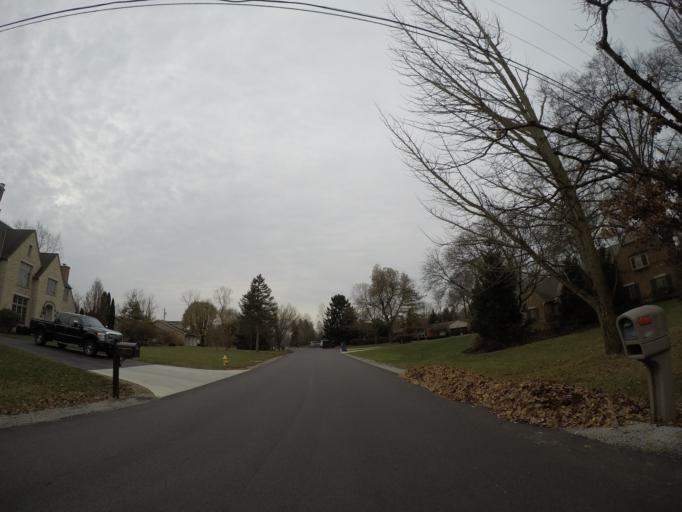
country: US
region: Ohio
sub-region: Franklin County
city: Dublin
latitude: 40.0583
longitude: -83.0847
